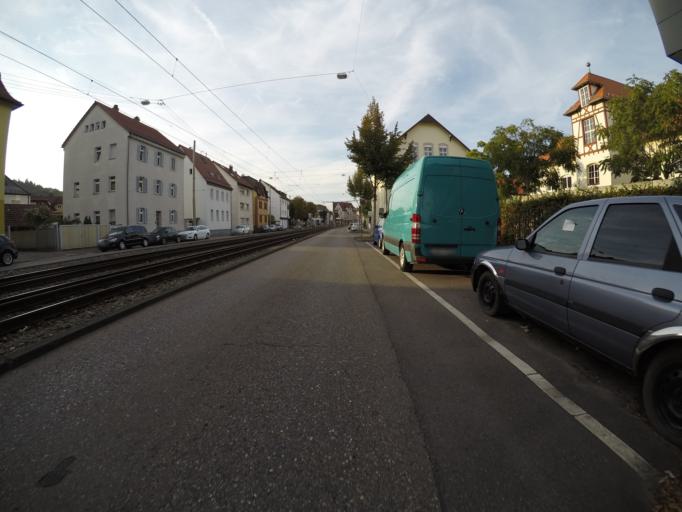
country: DE
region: Baden-Wuerttemberg
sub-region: Regierungsbezirk Stuttgart
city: Stuttgart-Ost
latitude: 48.7706
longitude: 9.2463
